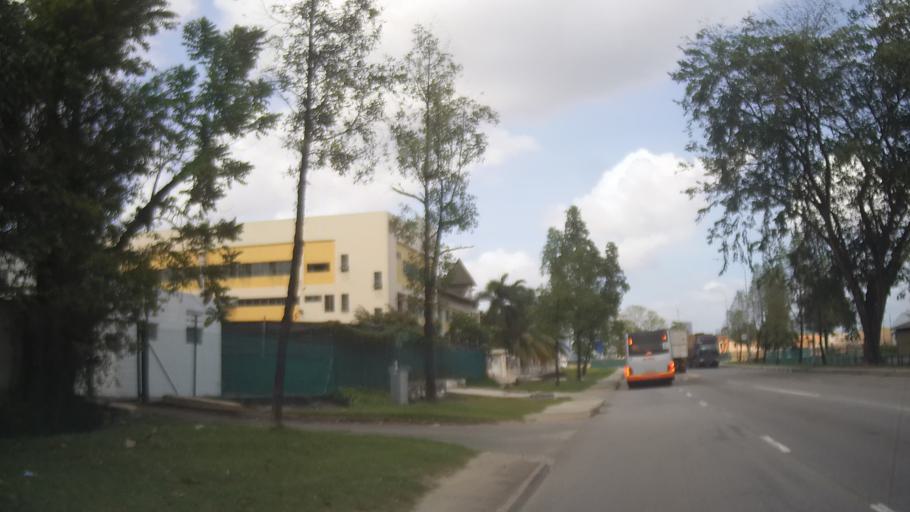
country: MY
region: Johor
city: Johor Bahru
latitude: 1.4342
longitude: 103.7487
